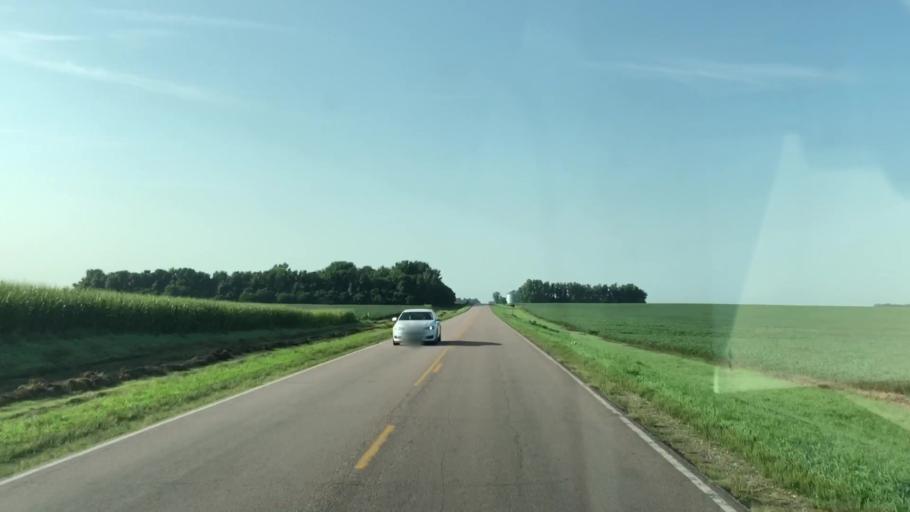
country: US
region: Iowa
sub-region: Lyon County
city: George
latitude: 43.3255
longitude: -95.9988
